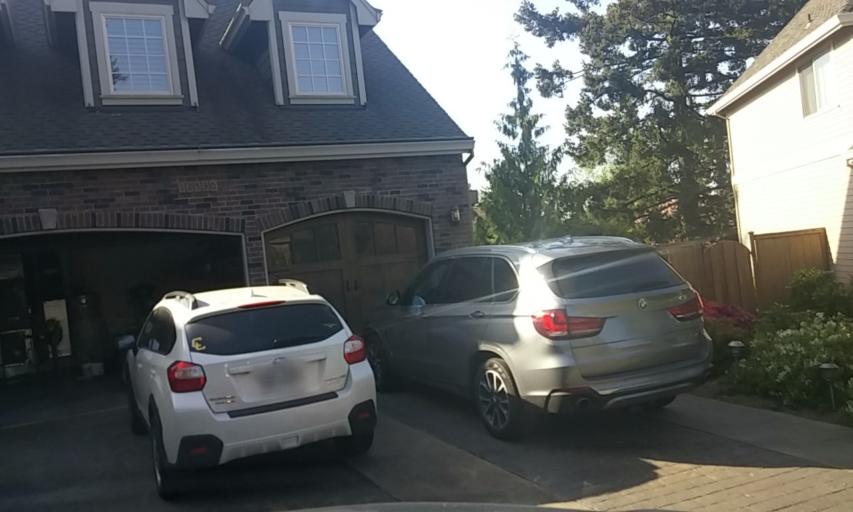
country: US
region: Oregon
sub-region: Washington County
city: Metzger
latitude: 45.4348
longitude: -122.7391
